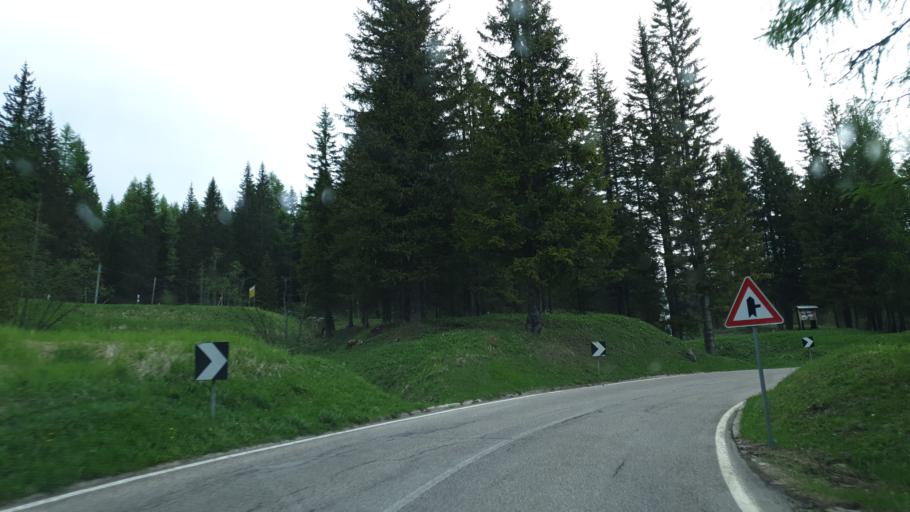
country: IT
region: Veneto
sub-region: Provincia di Belluno
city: Cortina d'Ampezzo
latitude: 46.5642
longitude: 12.2432
